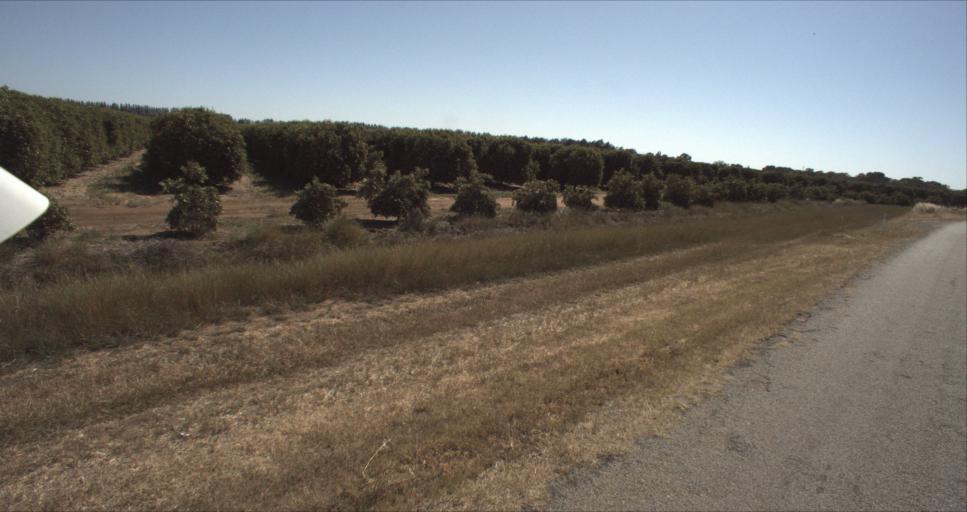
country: AU
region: New South Wales
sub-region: Leeton
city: Leeton
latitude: -34.5337
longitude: 146.3248
